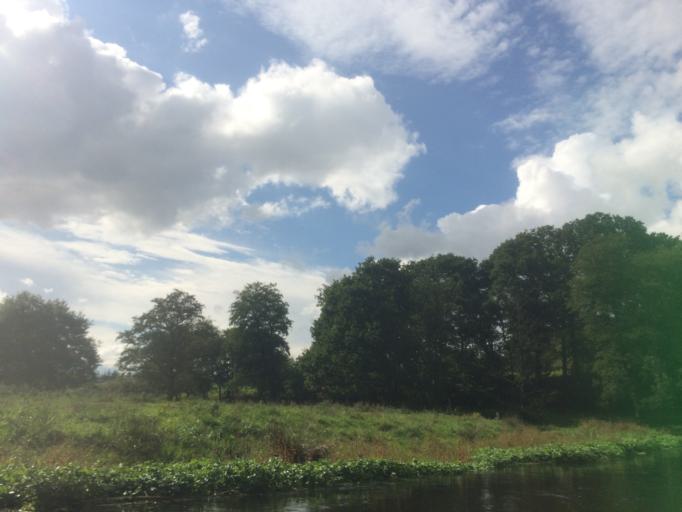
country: DK
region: South Denmark
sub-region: Vejle Kommune
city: Egtved
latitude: 55.6522
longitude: 9.3103
